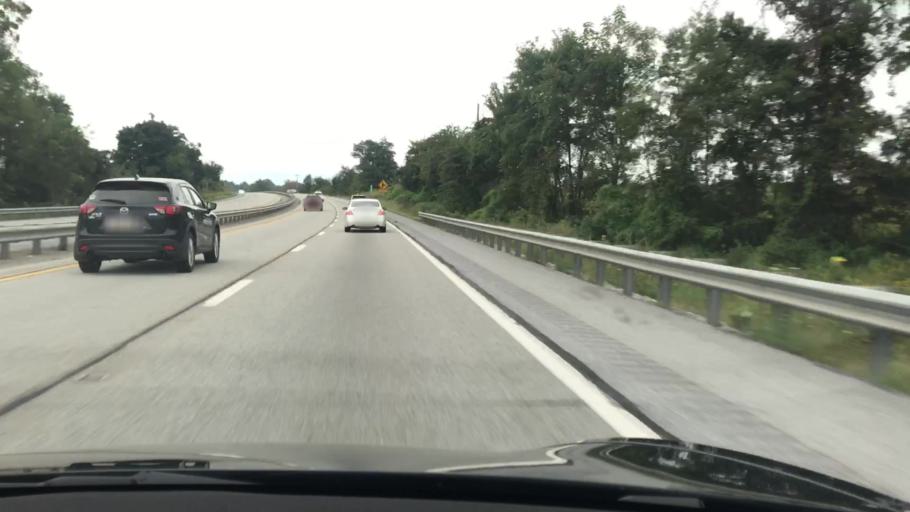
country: US
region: Pennsylvania
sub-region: Adams County
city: Lake Meade
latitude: 40.0164
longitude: -77.0982
